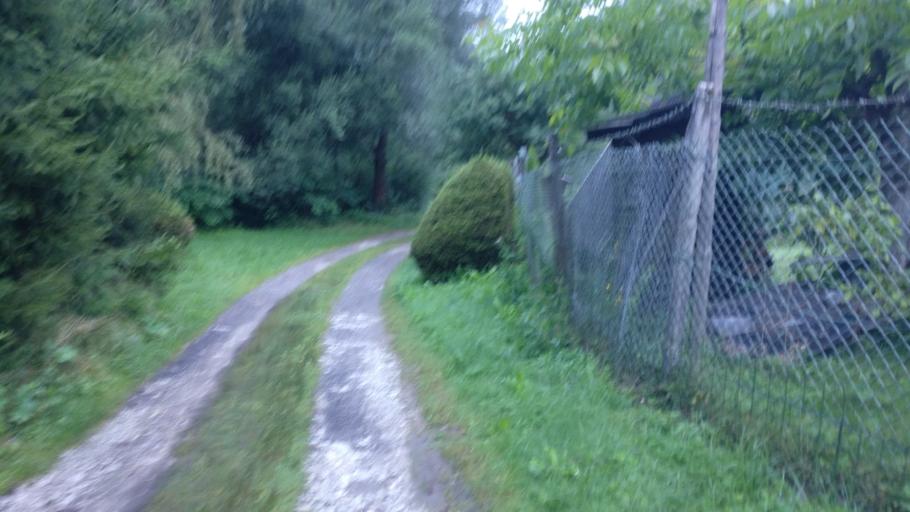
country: SK
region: Zilinsky
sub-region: Okres Zilina
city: Zilina
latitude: 49.2435
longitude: 18.7552
